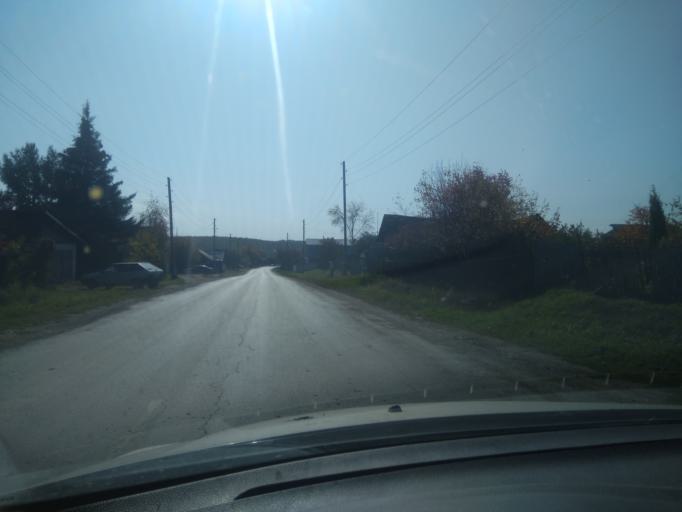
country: RU
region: Sverdlovsk
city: Pokrovskoye
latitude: 56.4417
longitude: 61.6023
